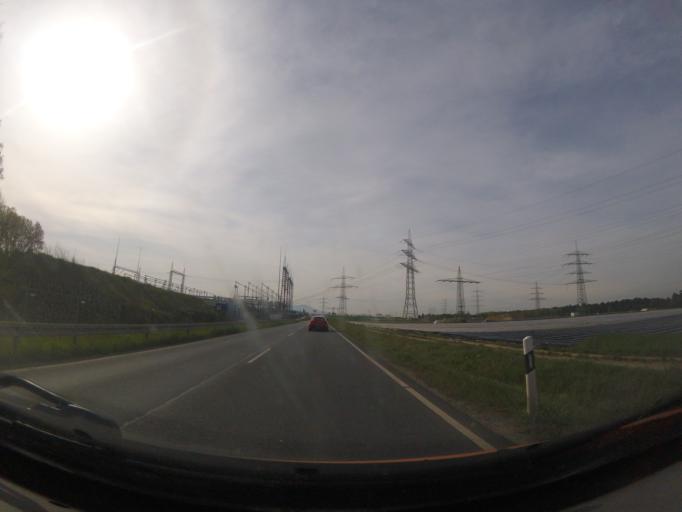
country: DE
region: Hesse
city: Pfungstadt
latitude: 49.8182
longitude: 8.5860
